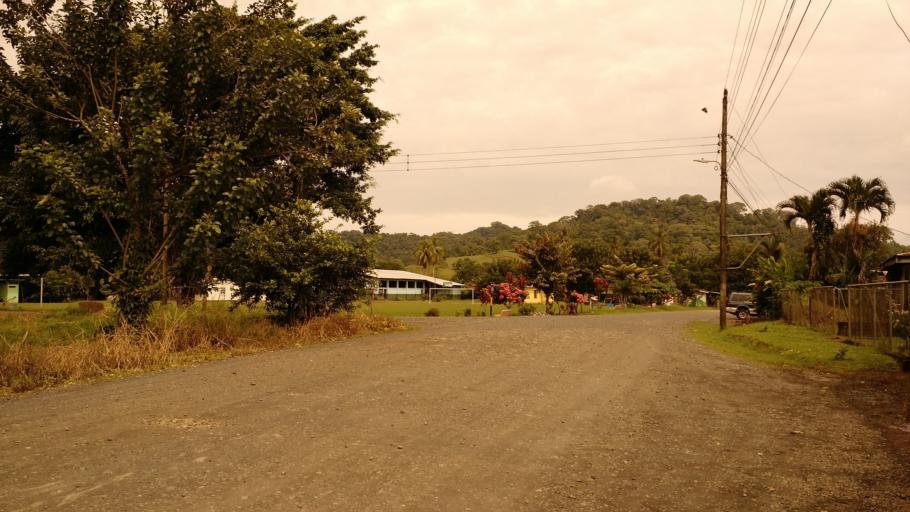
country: CR
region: Alajuela
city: Pital
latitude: 10.6763
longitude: -84.2313
